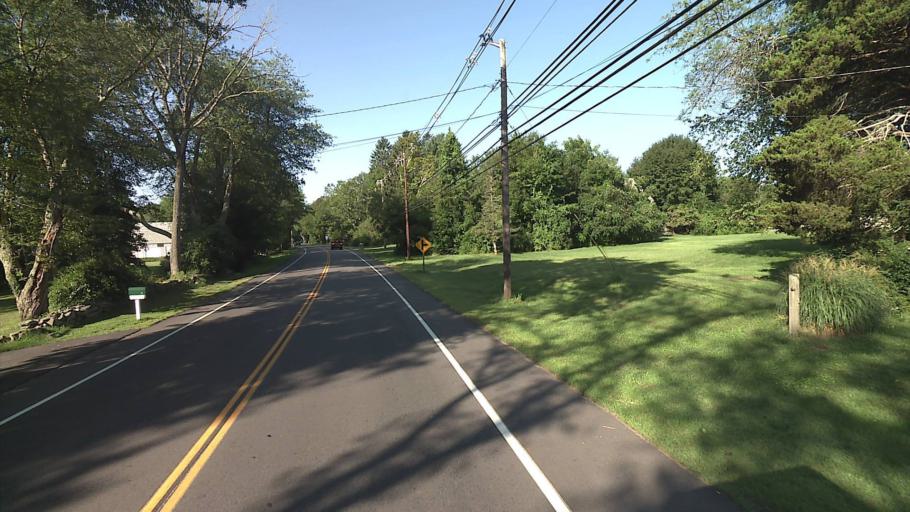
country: US
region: Connecticut
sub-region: Middlesex County
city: Old Saybrook Center
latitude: 41.3338
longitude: -72.3188
